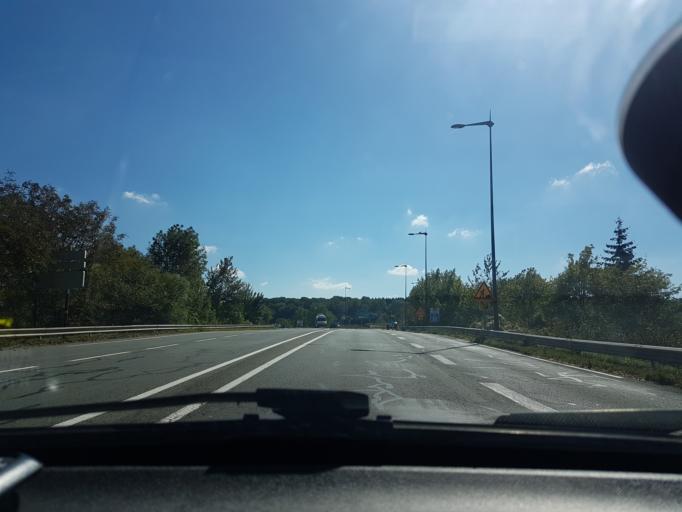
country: FR
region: Franche-Comte
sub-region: Territoire de Belfort
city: Belfort
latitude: 47.6379
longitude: 6.8794
